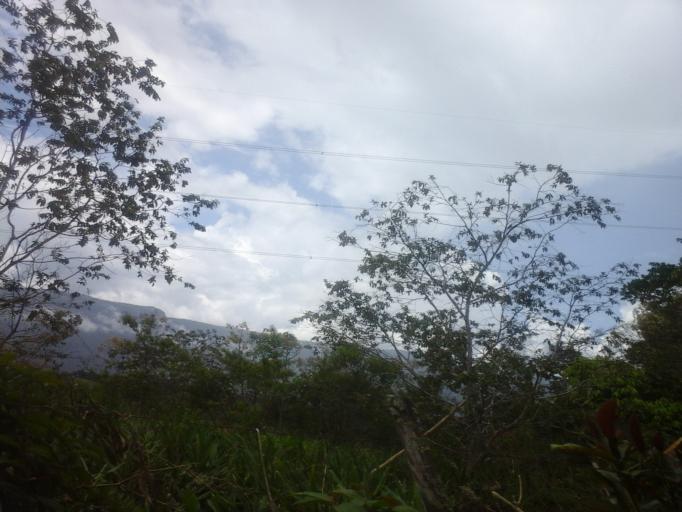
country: CO
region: Putumayo
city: Mocoa
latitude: 1.1744
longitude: -76.6607
